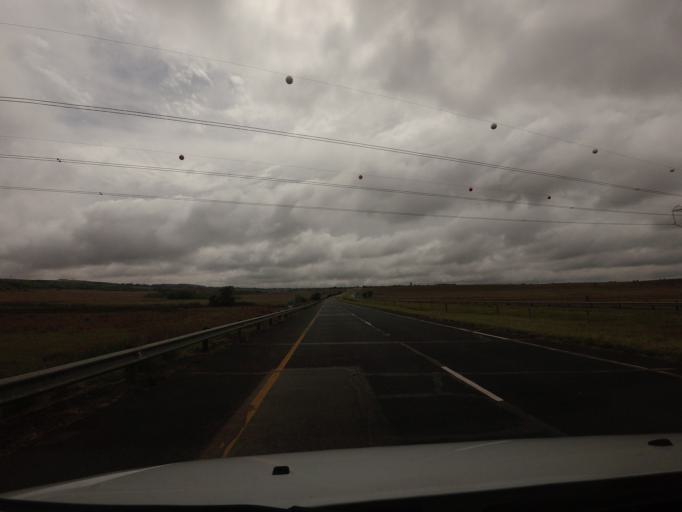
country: ZA
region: Mpumalanga
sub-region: Nkangala District Municipality
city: Middelburg
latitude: -25.8512
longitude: 29.3885
